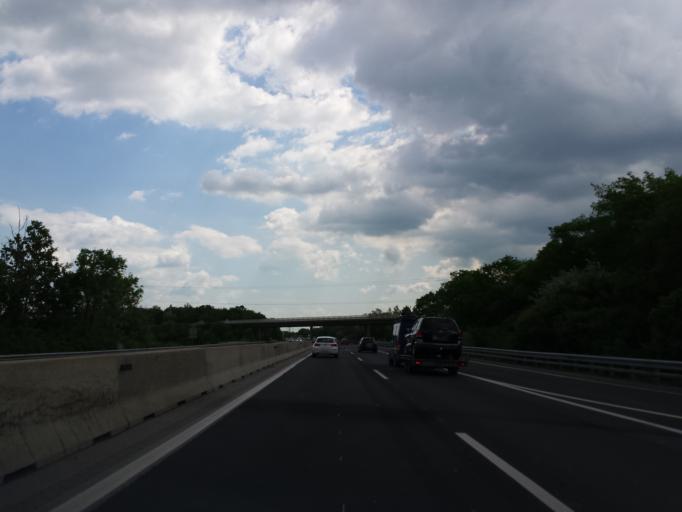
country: AT
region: Lower Austria
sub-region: Politischer Bezirk Bruck an der Leitha
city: Bruck an der Leitha
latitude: 48.0445
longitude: 16.7551
